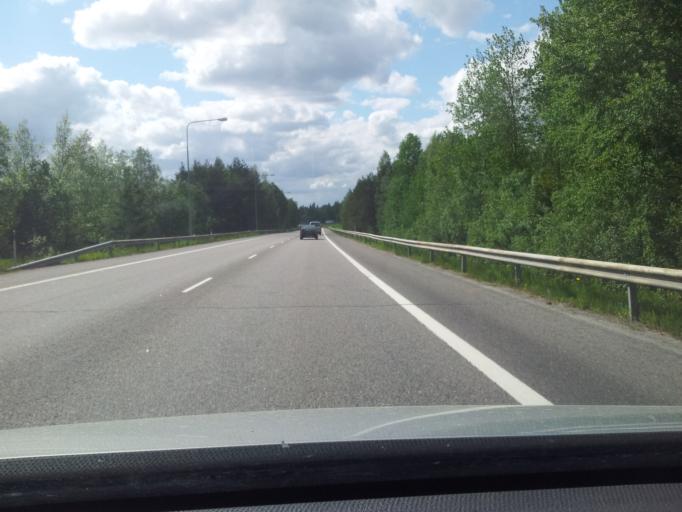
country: FI
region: Kymenlaakso
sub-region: Kouvola
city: Kouvola
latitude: 60.8729
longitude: 26.6318
